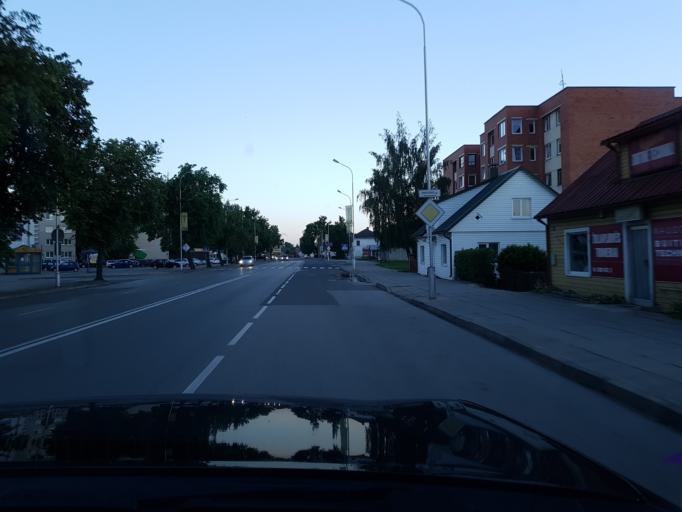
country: LT
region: Marijampoles apskritis
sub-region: Marijampole Municipality
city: Marijampole
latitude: 54.5643
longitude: 23.3558
